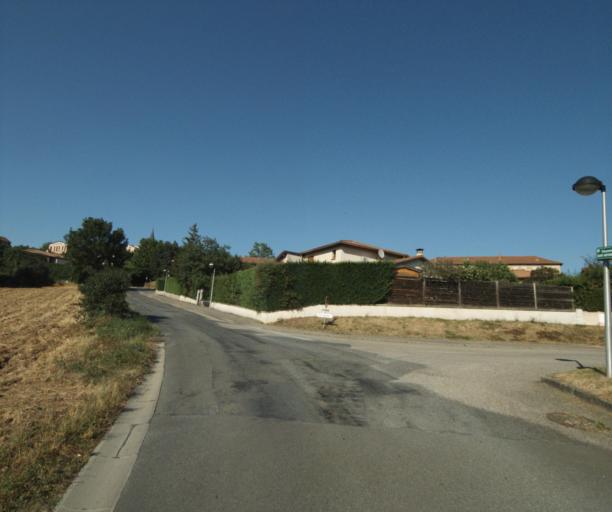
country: FR
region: Rhone-Alpes
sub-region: Departement du Rhone
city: Saint-Pierre-la-Palud
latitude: 45.7884
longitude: 4.6103
